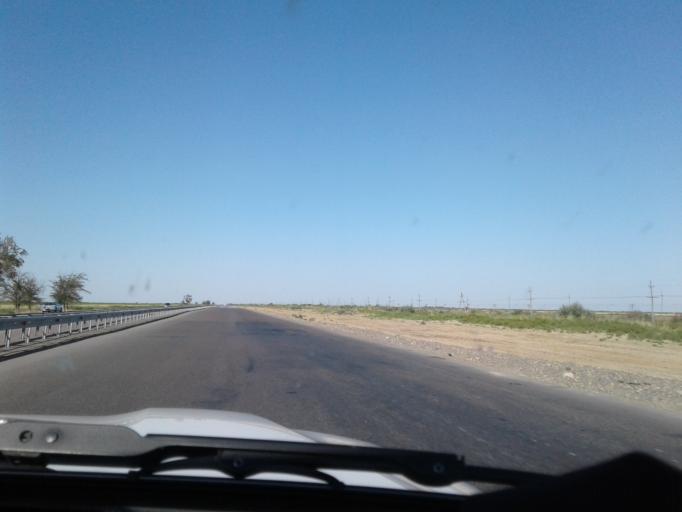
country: TM
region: Ahal
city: Tejen
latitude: 37.2518
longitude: 60.1966
